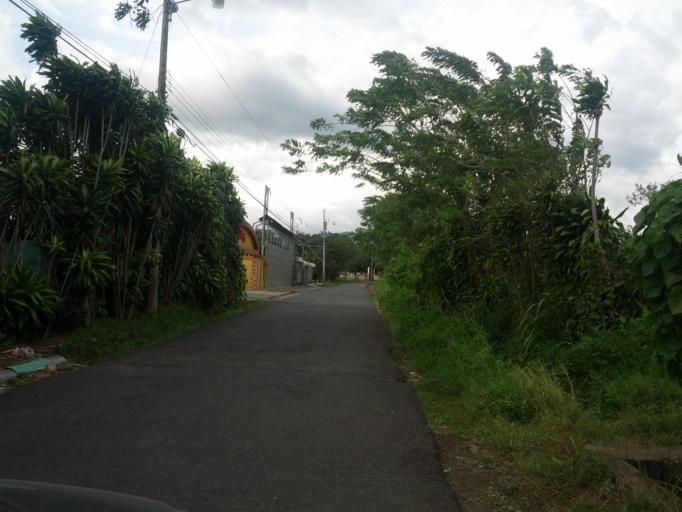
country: CR
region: Heredia
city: Llorente
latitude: 10.0206
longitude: -84.1756
